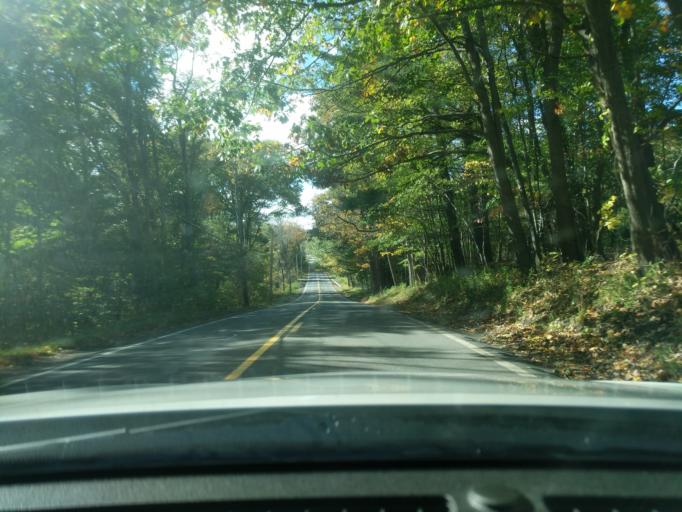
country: US
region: Massachusetts
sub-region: Berkshire County
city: Otis
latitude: 42.1722
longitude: -72.9980
